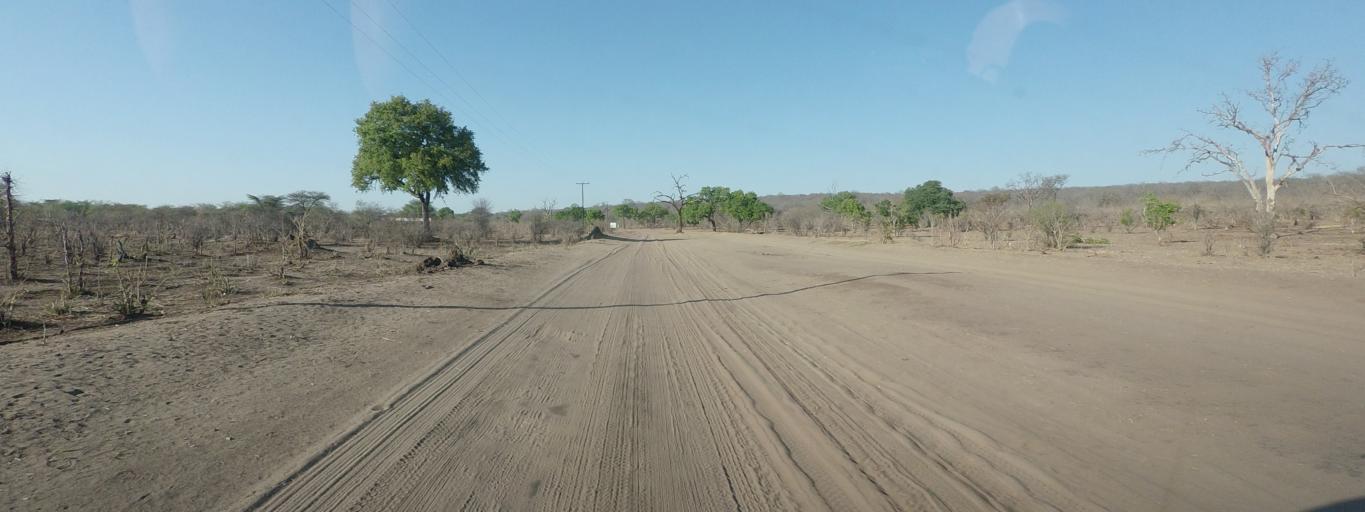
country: BW
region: North West
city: Kasane
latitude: -17.8855
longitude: 25.2308
